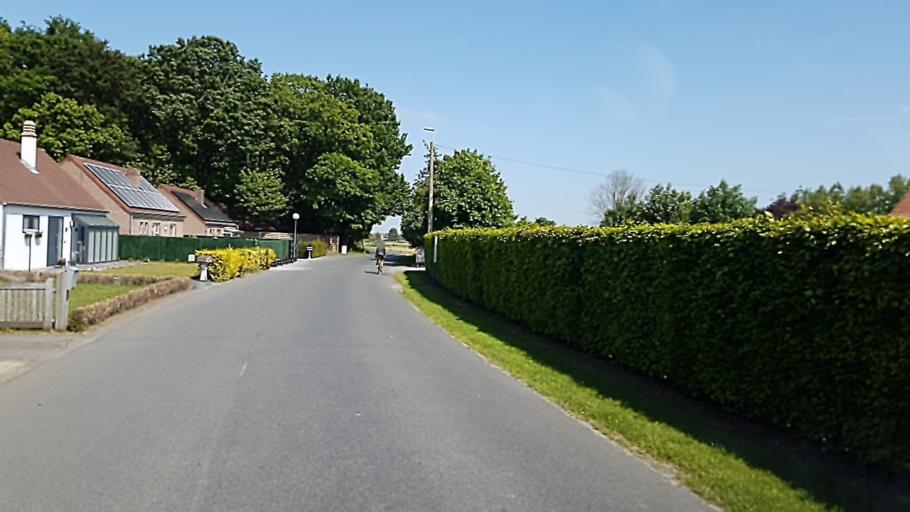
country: BE
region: Flanders
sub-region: Provincie West-Vlaanderen
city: Zonnebeke
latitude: 50.8459
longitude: 2.9675
